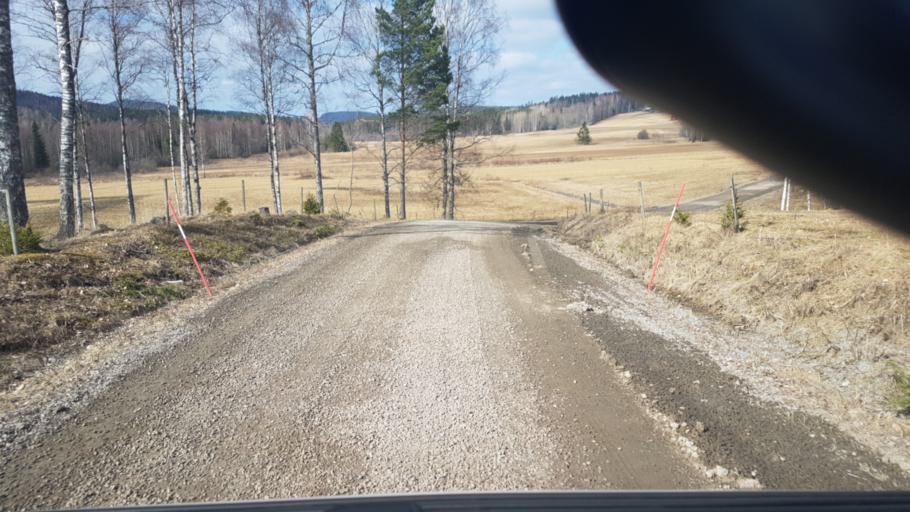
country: SE
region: Vaermland
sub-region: Eda Kommun
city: Amotfors
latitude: 59.7833
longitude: 12.4375
